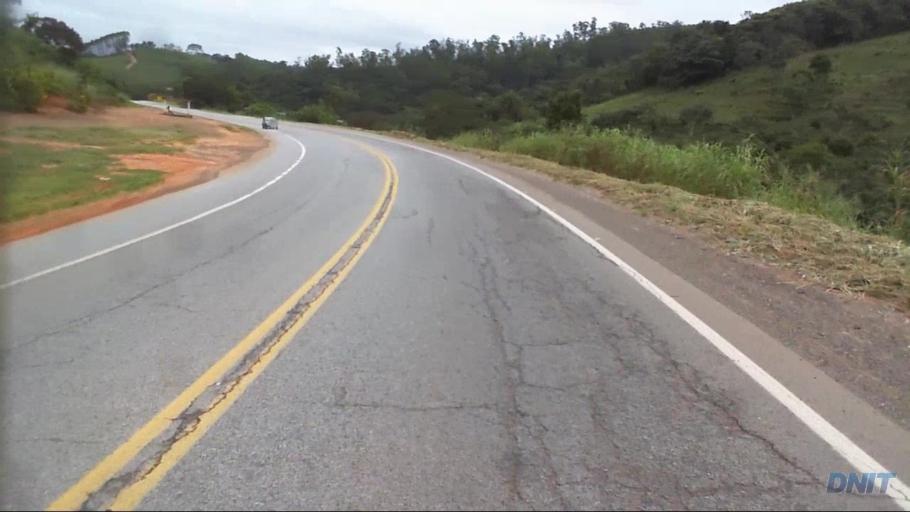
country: BR
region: Minas Gerais
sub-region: Joao Monlevade
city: Joao Monlevade
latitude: -19.8484
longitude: -43.2534
